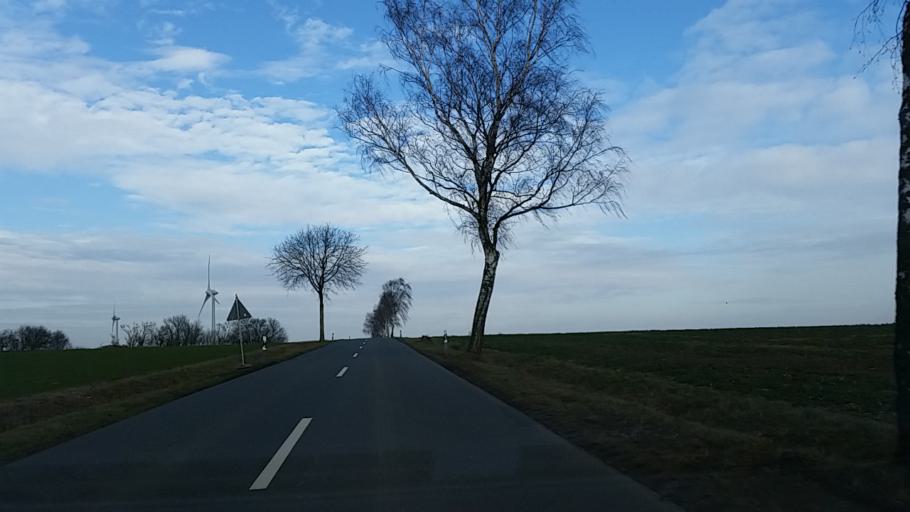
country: DE
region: Lower Saxony
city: Romstedt
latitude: 53.1200
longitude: 10.6407
